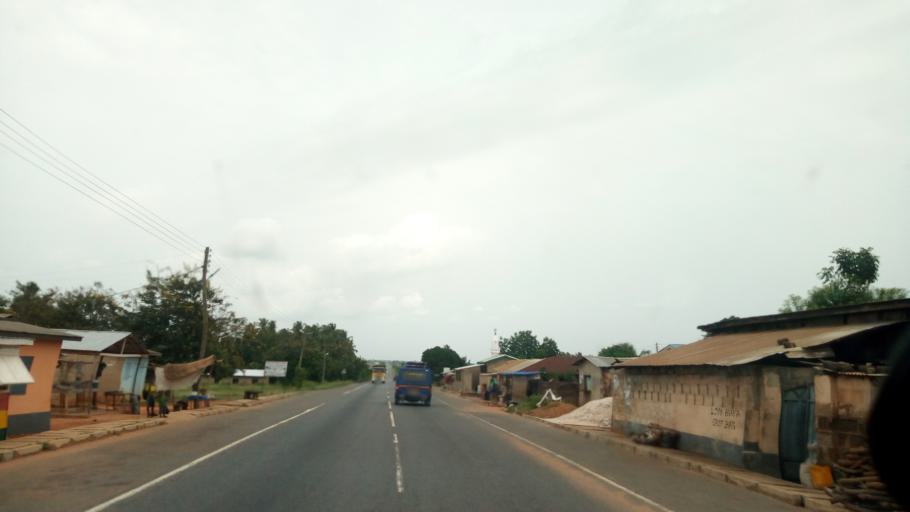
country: GH
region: Volta
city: Keta
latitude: 6.0642
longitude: 0.9188
